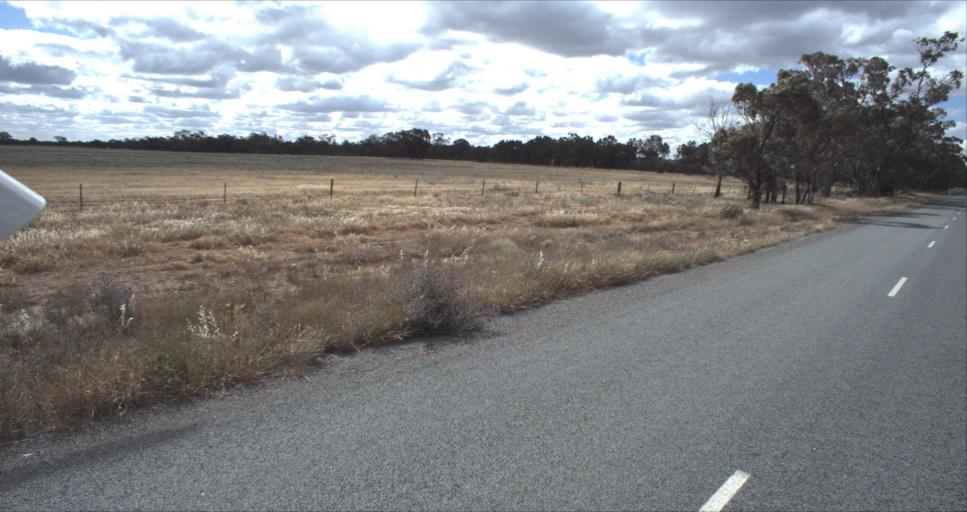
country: AU
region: New South Wales
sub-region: Leeton
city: Leeton
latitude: -34.6688
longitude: 146.3479
